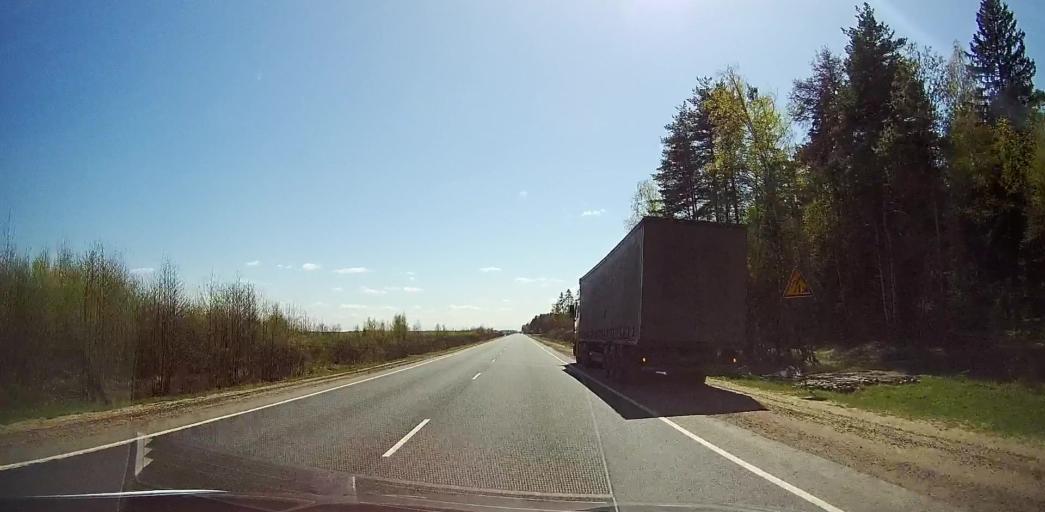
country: RU
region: Moskovskaya
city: Gzhel'
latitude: 55.5993
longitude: 38.3790
